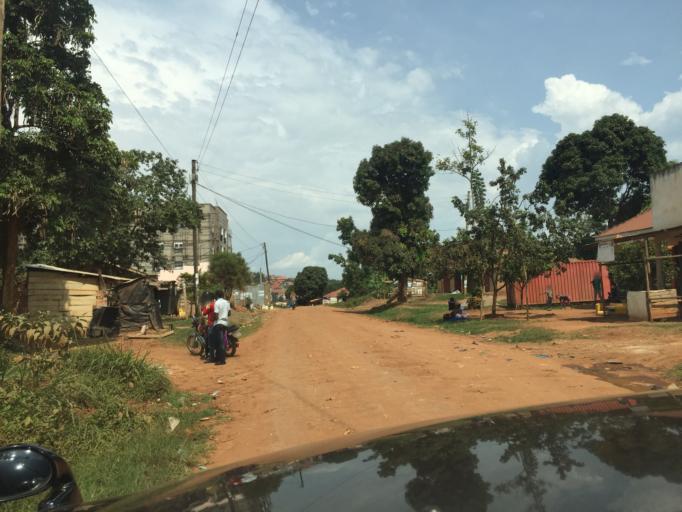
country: UG
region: Central Region
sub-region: Wakiso District
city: Kireka
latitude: 0.4135
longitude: 32.6226
